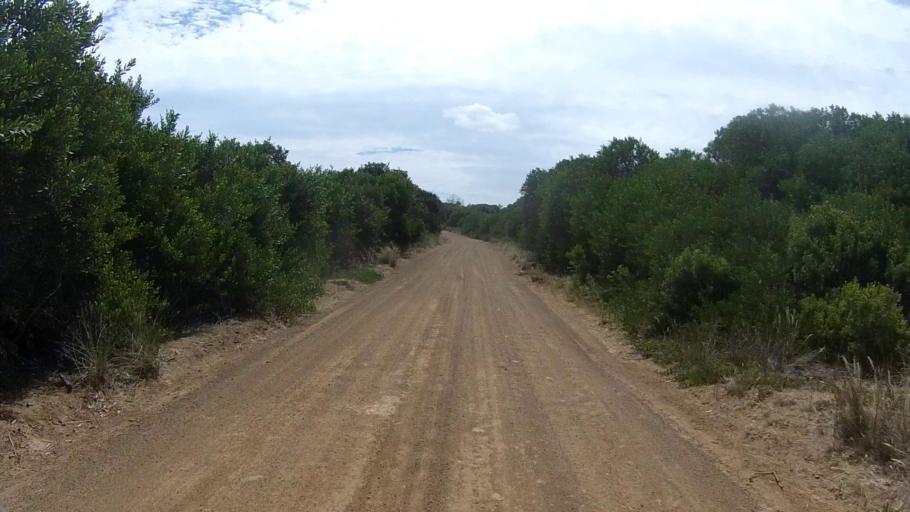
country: AU
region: Tasmania
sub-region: Clarence
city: Sandford
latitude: -43.0229
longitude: 147.4924
